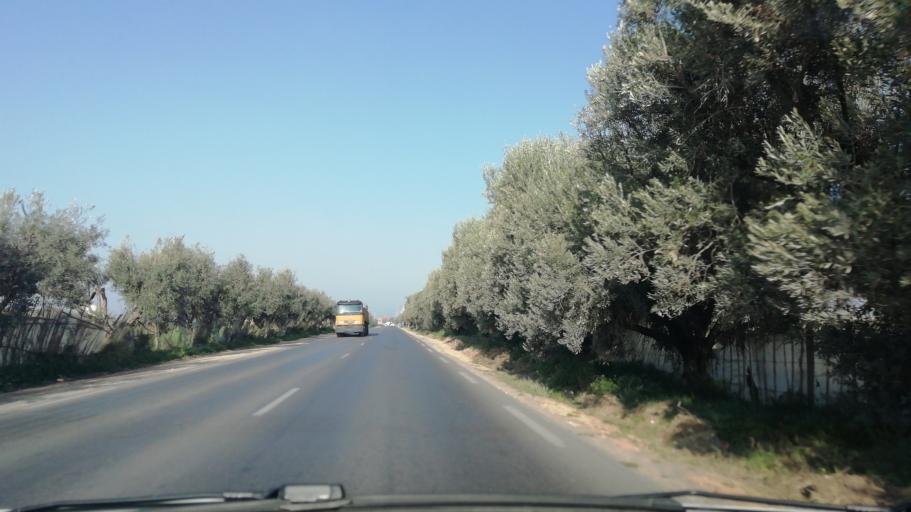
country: DZ
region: Mostaganem
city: Mostaganem
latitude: 35.7503
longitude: 0.1263
